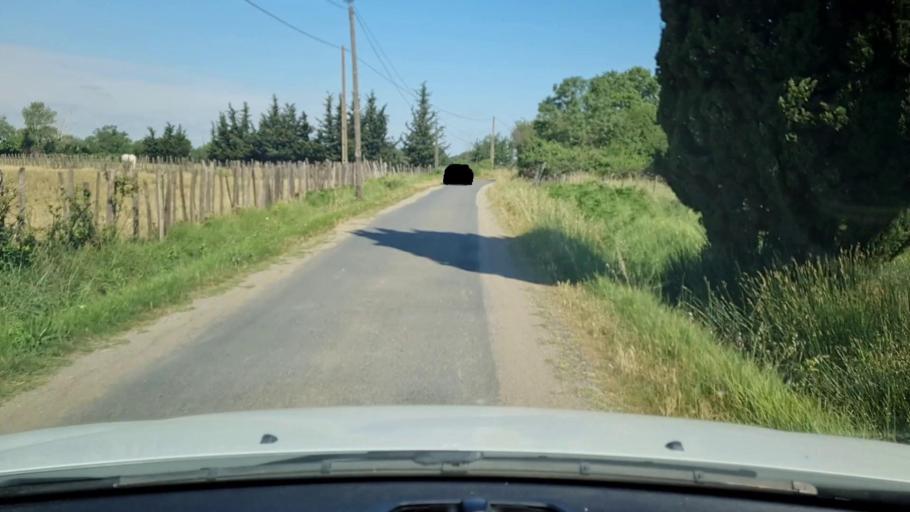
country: FR
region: Languedoc-Roussillon
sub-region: Departement du Gard
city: Le Cailar
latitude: 43.6527
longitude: 4.2381
